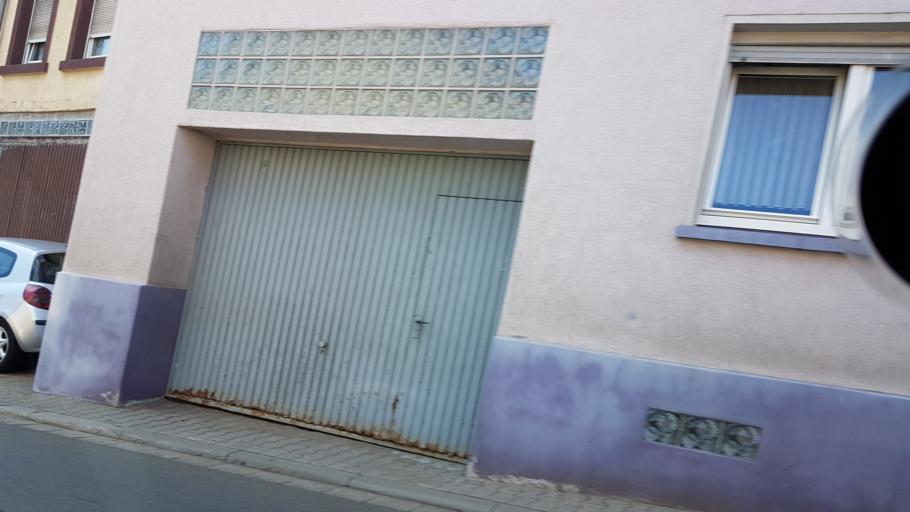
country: DE
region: Rheinland-Pfalz
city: Medard
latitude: 49.6674
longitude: 7.6149
